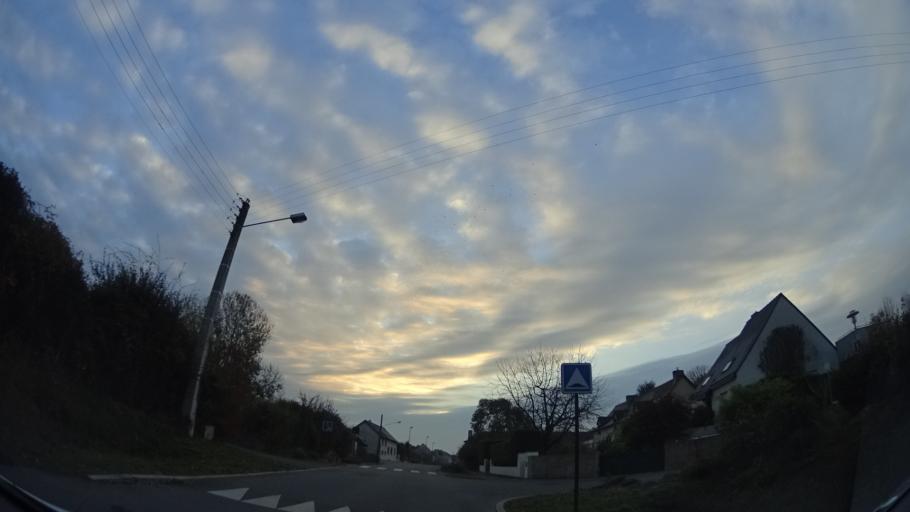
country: FR
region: Brittany
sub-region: Departement d'Ille-et-Vilaine
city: La Meziere
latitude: 48.2018
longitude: -1.7384
